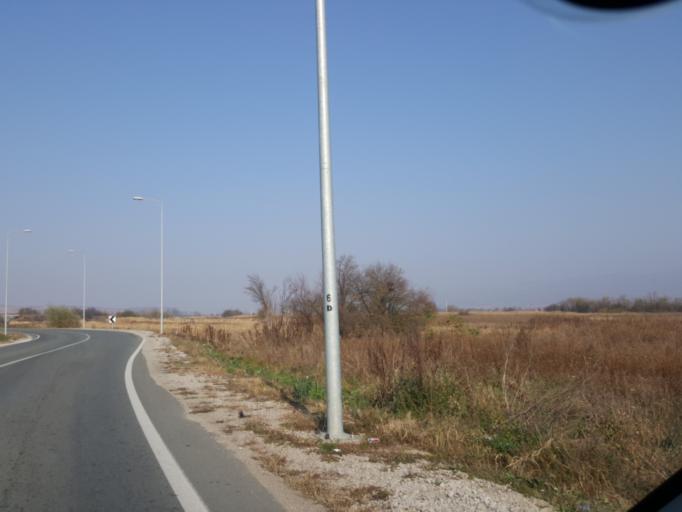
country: RS
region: Central Serbia
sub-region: Jablanicki Okrug
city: Leskovac
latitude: 43.0289
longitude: 21.9436
